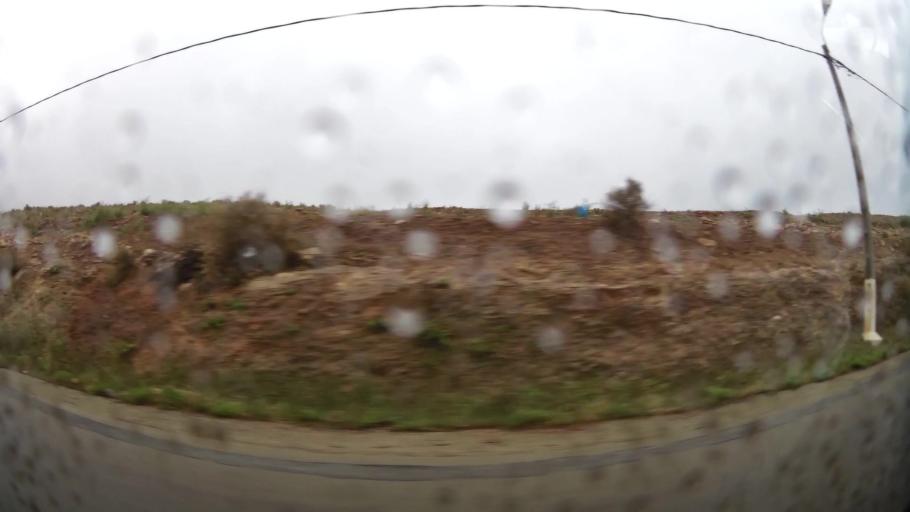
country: MA
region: Taza-Al Hoceima-Taounate
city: Tirhanimine
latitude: 35.2417
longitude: -3.9634
